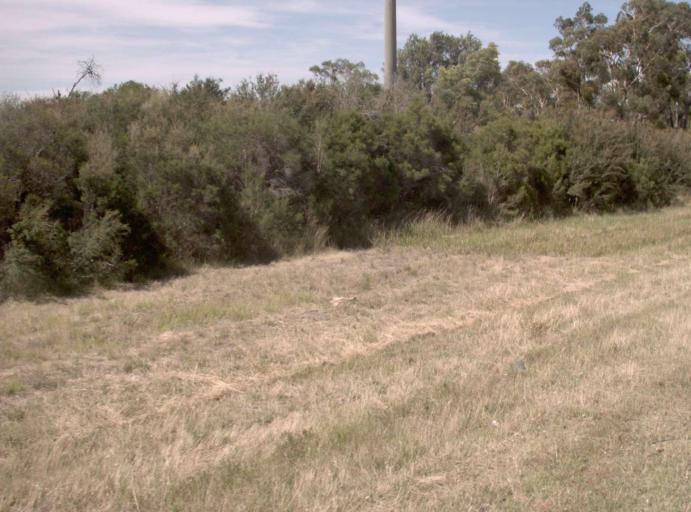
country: AU
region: Victoria
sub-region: Wellington
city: Sale
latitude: -38.1612
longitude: 146.9107
